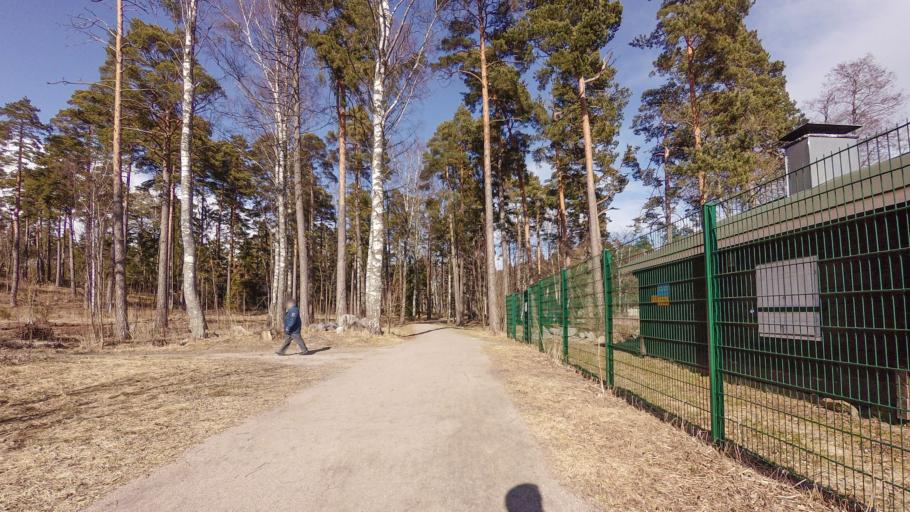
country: FI
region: Uusimaa
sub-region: Helsinki
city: Vantaa
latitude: 60.1984
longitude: 25.1288
